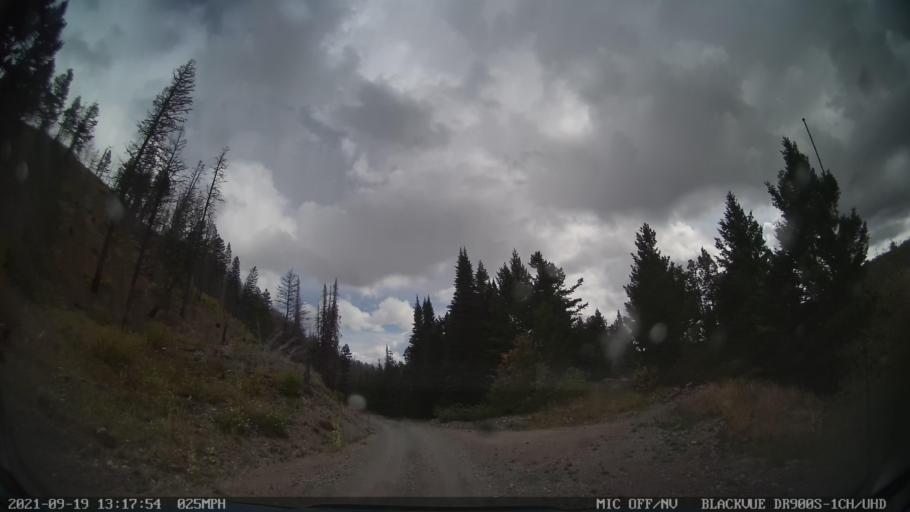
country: US
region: Montana
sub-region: Missoula County
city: Seeley Lake
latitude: 47.1724
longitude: -113.3606
